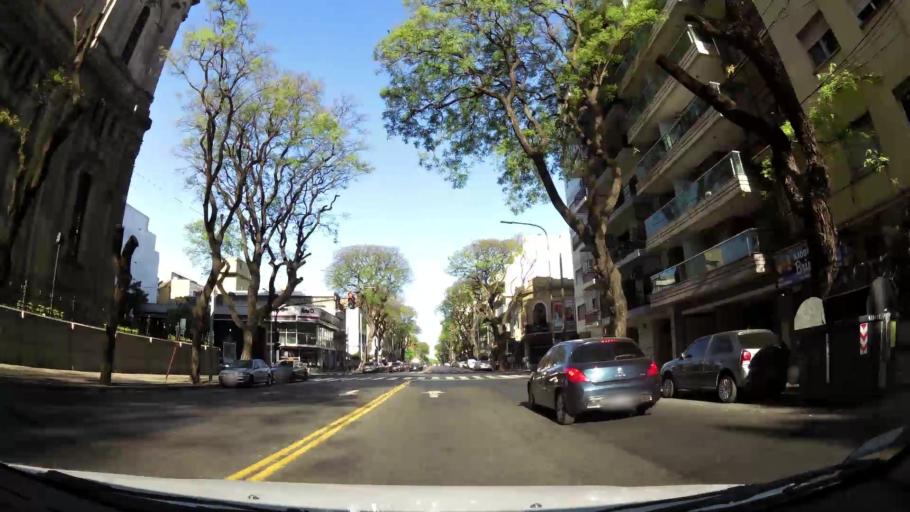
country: AR
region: Buenos Aires F.D.
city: Villa Santa Rita
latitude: -34.6258
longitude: -58.4332
